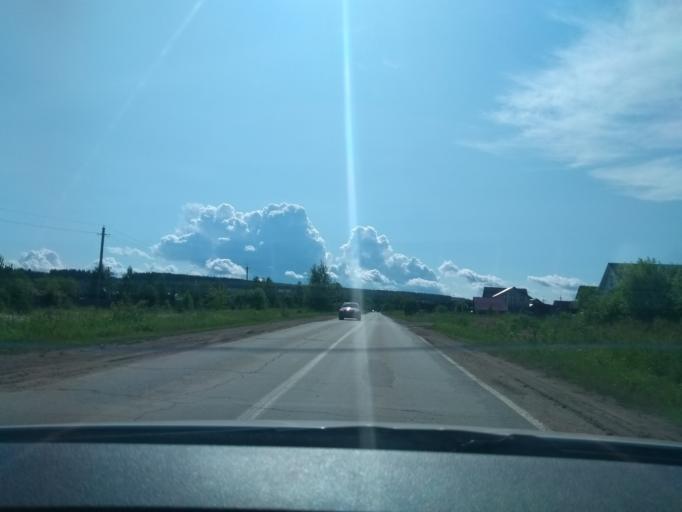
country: RU
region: Perm
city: Lobanovo
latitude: 57.8436
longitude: 56.3628
